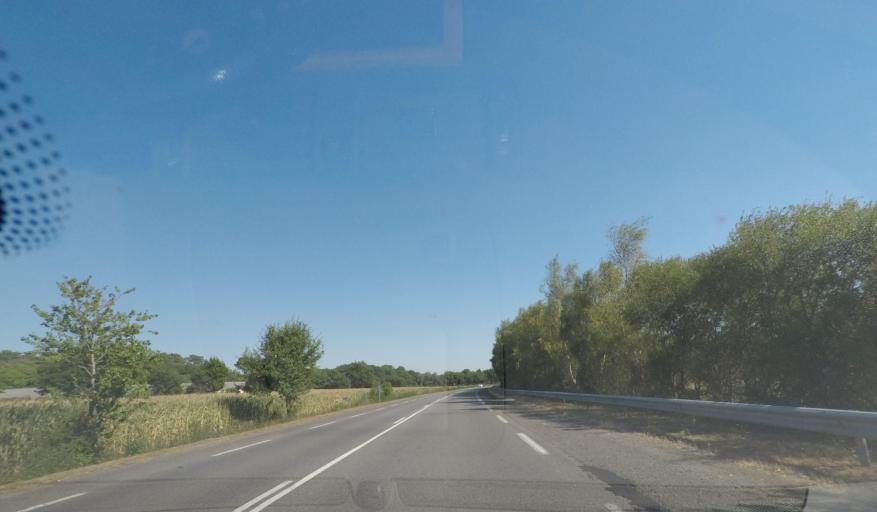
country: FR
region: Brittany
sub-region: Departement du Morbihan
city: Limerzel
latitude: 47.6120
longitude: -2.3914
